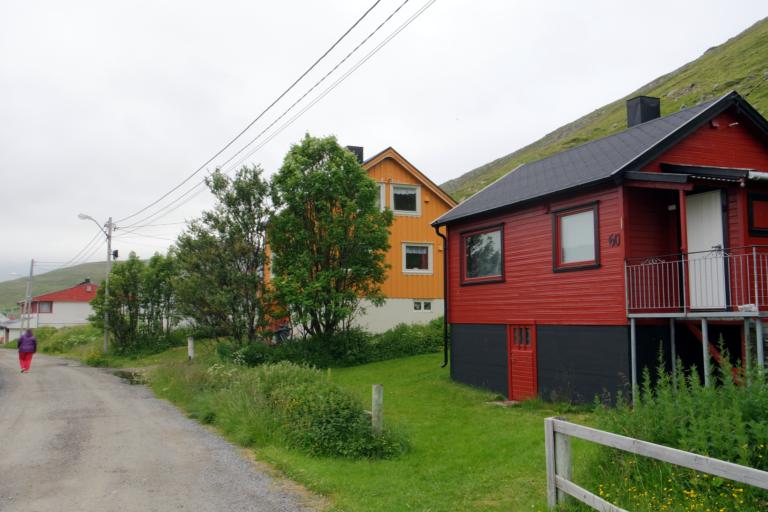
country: NO
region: Finnmark Fylke
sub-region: Nordkapp
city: Honningsvag
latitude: 71.1146
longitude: 25.8349
